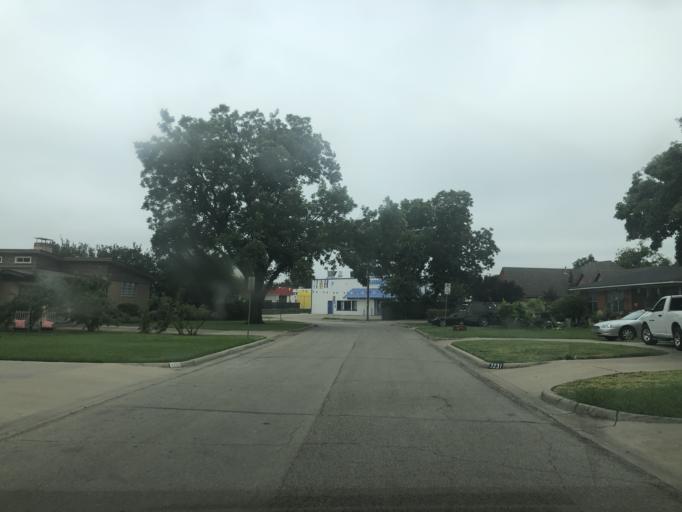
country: US
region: Texas
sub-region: Dallas County
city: University Park
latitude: 32.8563
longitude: -96.8668
